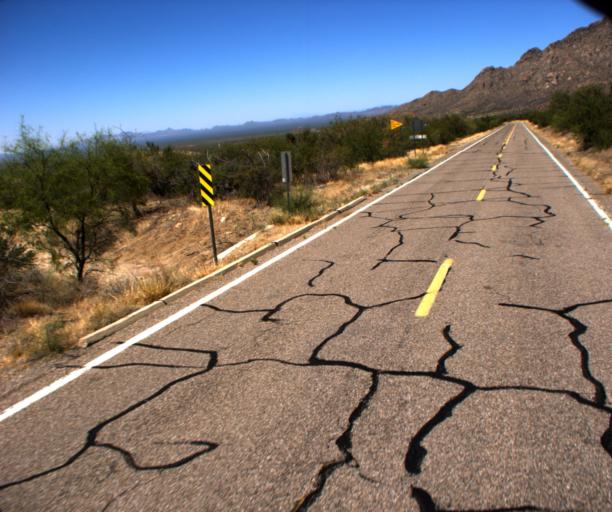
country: US
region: Arizona
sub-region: Pima County
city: Three Points
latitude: 31.9932
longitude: -111.5750
